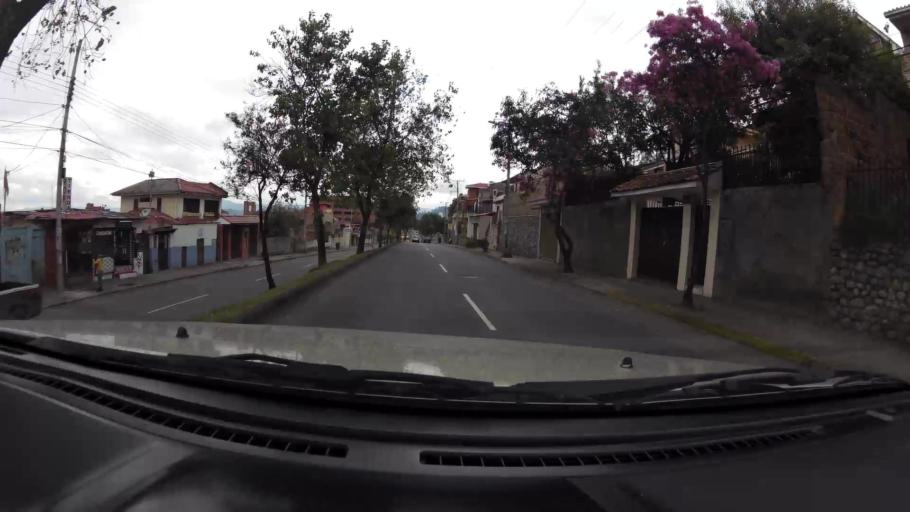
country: EC
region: Azuay
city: Cuenca
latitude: -2.9091
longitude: -79.0149
